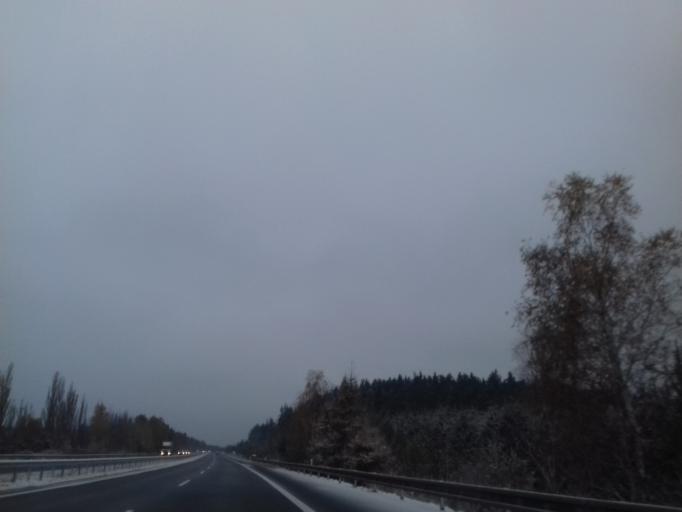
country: CZ
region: Plzensky
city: Myto
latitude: 49.8130
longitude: 13.7597
